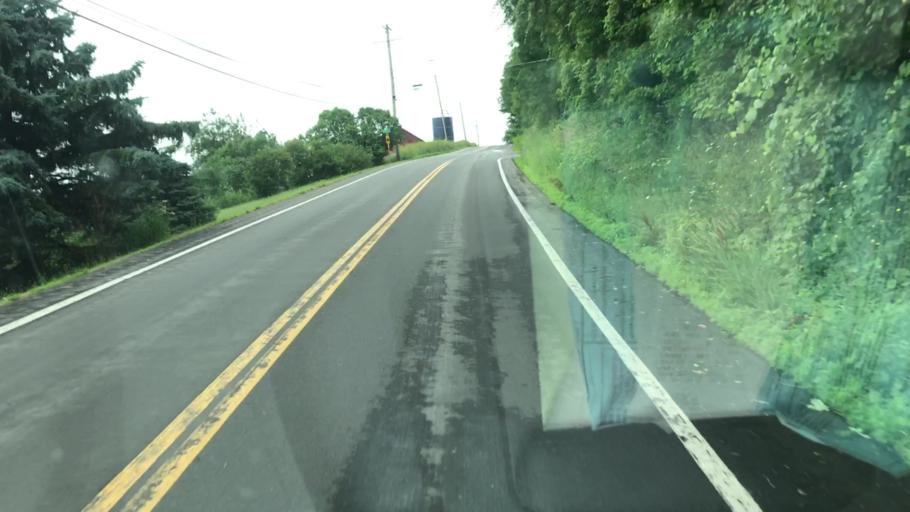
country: US
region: New York
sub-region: Onondaga County
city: Manlius
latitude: 42.9623
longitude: -75.9868
